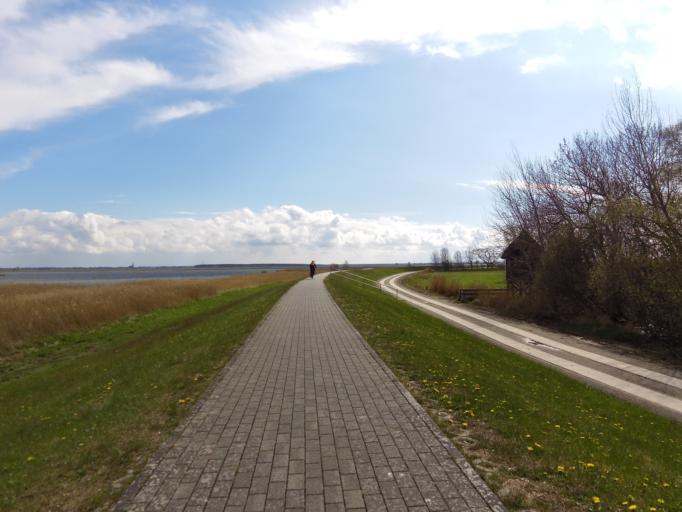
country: DE
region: Mecklenburg-Vorpommern
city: Zingst
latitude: 54.4319
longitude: 12.7175
